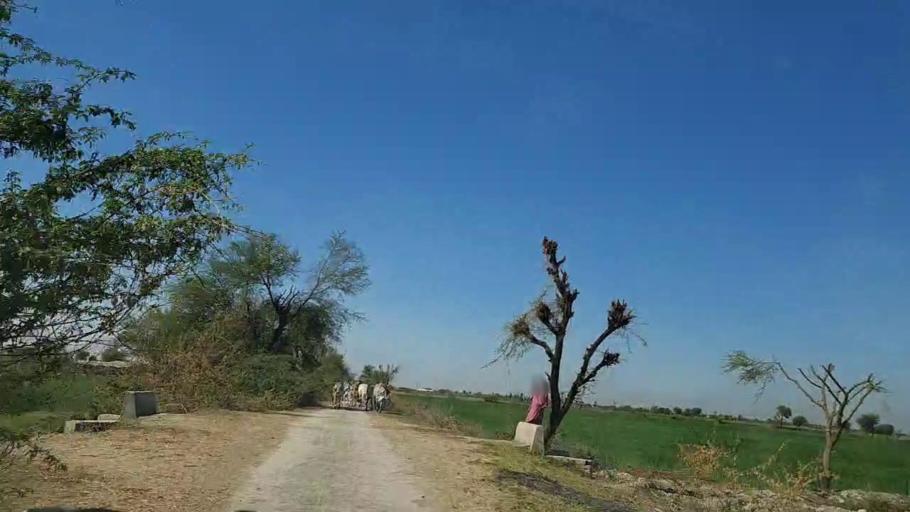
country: PK
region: Sindh
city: Dhoro Naro
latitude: 25.4889
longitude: 69.5200
